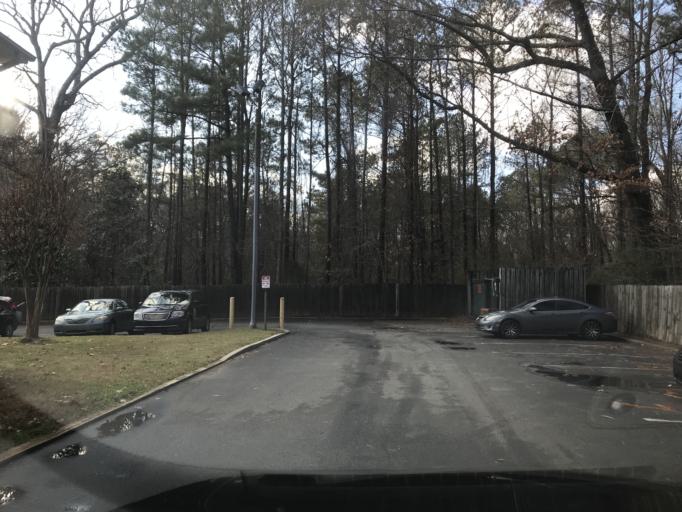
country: US
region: Georgia
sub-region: Fulton County
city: College Park
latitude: 33.6449
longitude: -84.4707
